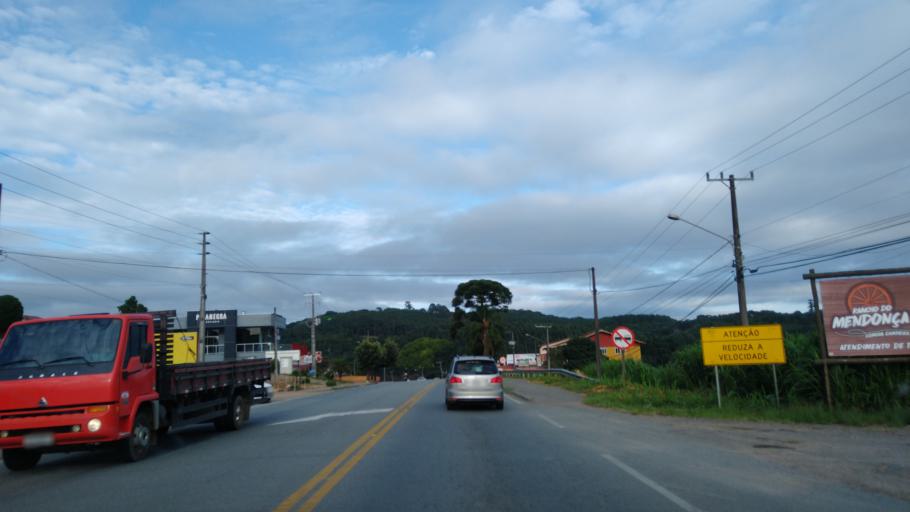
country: BR
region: Santa Catarina
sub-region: Sao Bento Do Sul
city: Sao Bento do Sul
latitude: -26.2244
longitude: -49.4129
